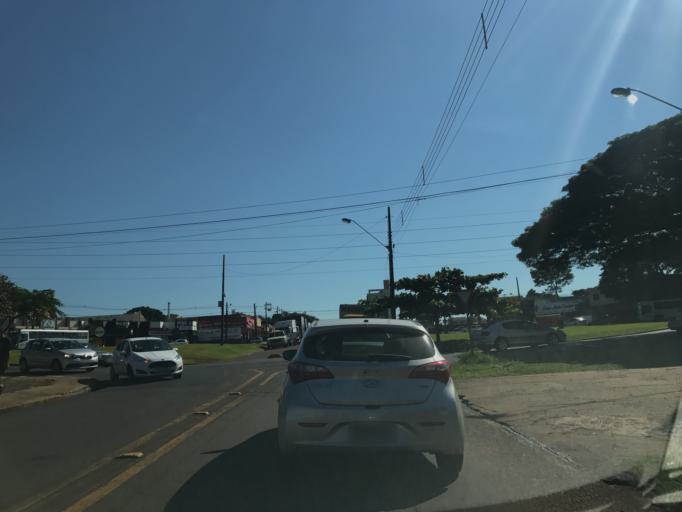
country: BR
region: Parana
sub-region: Maringa
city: Maringa
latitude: -23.4501
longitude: -51.9541
